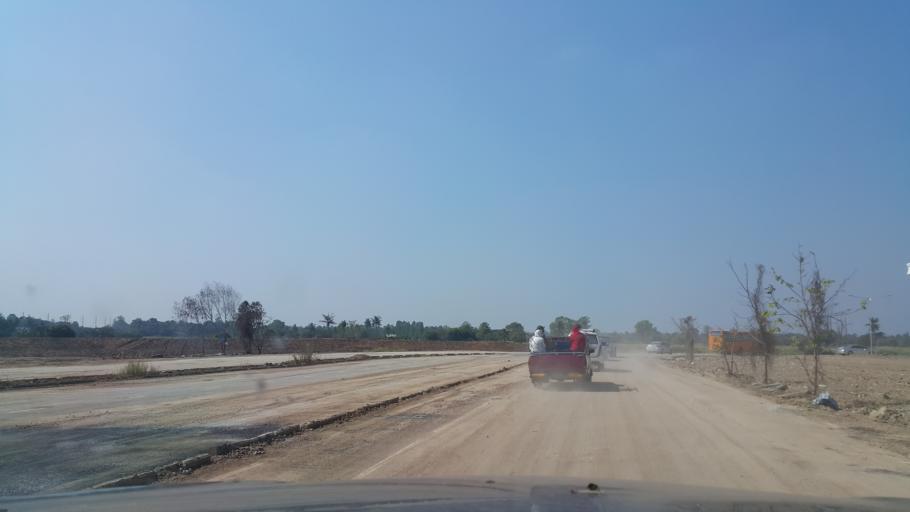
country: TH
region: Khon Kaen
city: Khon Kaen
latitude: 16.5119
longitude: 102.8680
